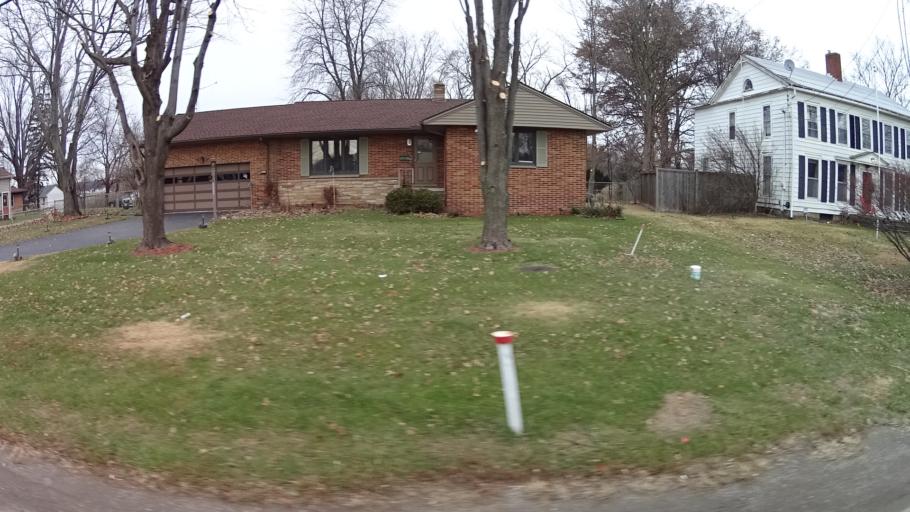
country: US
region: Ohio
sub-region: Lorain County
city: North Ridgeville
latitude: 41.3878
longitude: -82.0274
